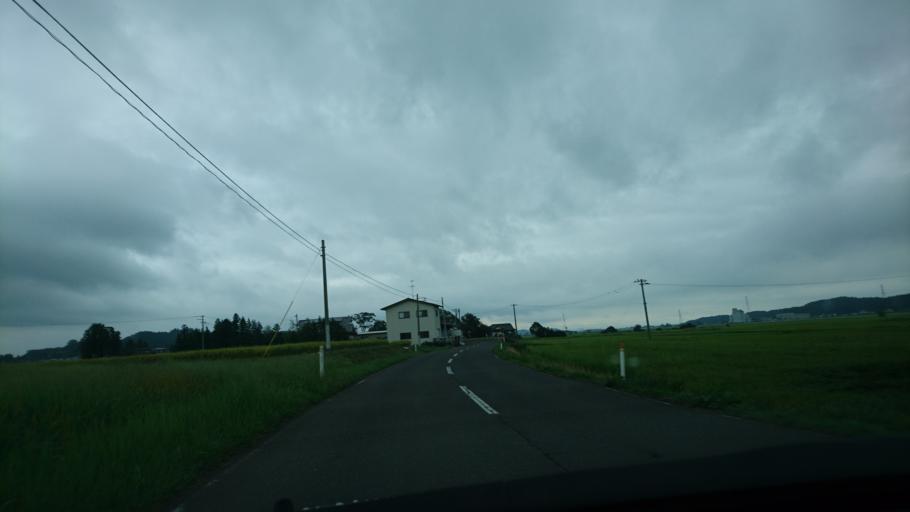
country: JP
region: Iwate
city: Ichinoseki
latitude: 38.8113
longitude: 140.9706
